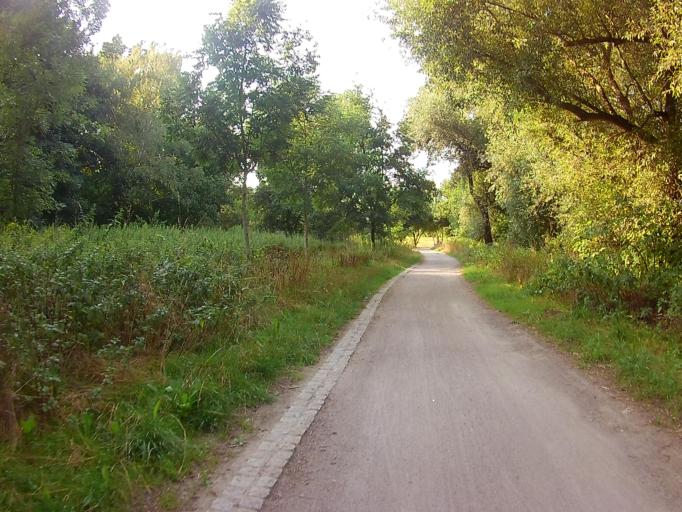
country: DE
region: Berlin
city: Kaulsdorf
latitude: 52.5098
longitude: 13.5735
